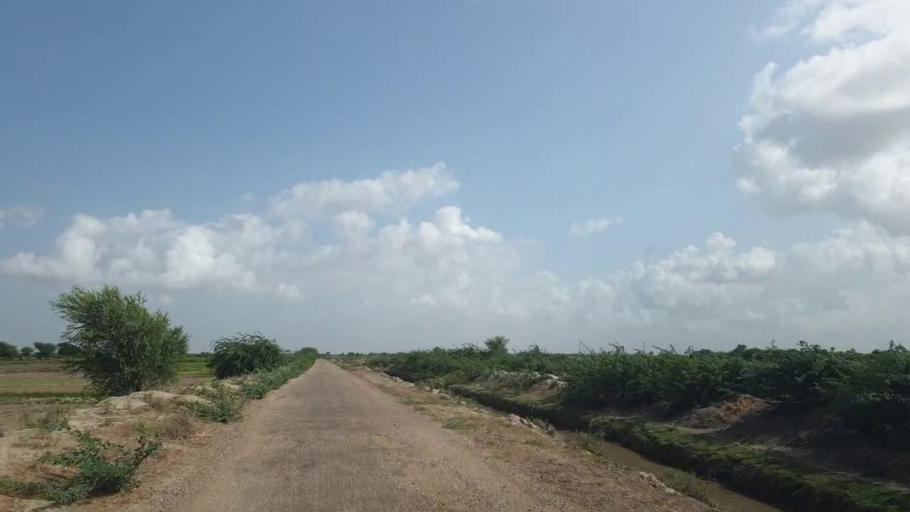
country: PK
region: Sindh
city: Kadhan
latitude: 24.5744
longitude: 69.0671
